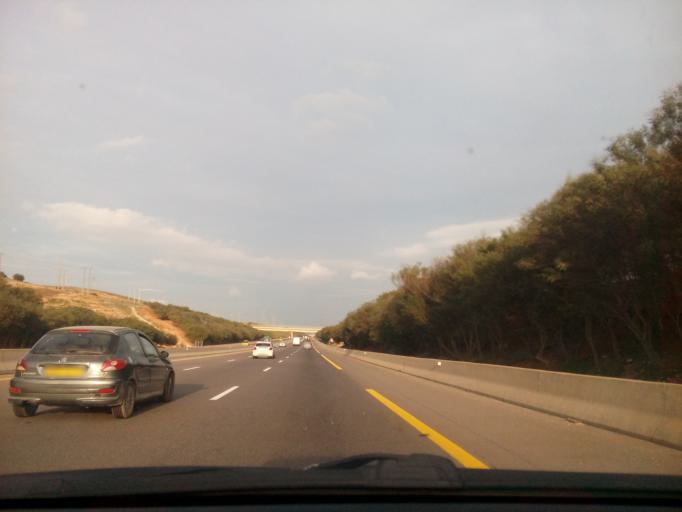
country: DZ
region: Relizane
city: Relizane
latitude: 35.7467
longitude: 0.3471
